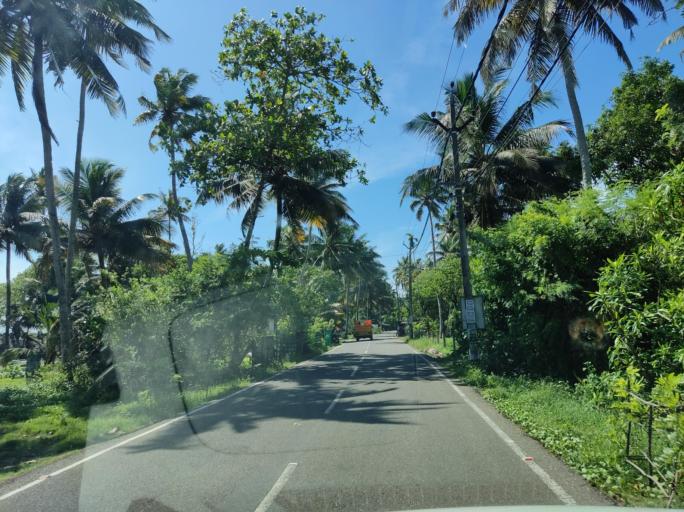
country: IN
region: Kerala
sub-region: Alappuzha
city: Kayankulam
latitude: 9.1769
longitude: 76.4450
